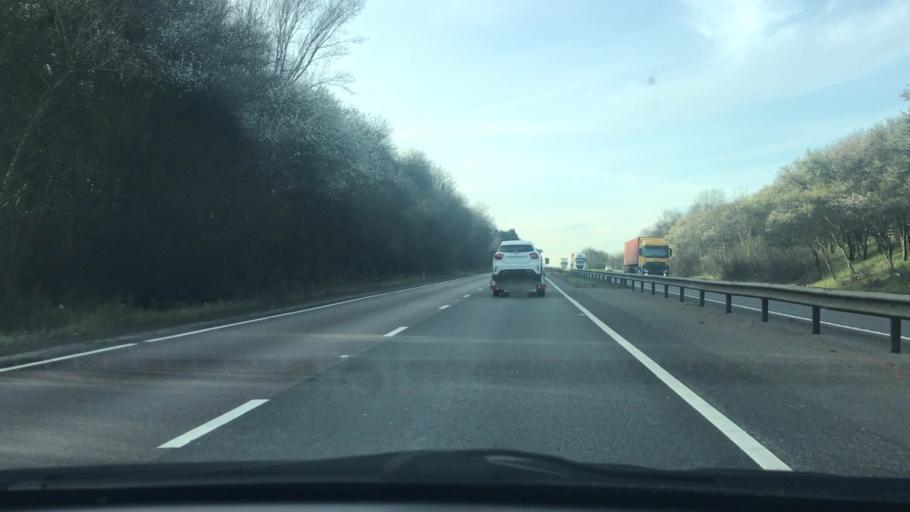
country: GB
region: England
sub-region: Nottinghamshire
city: Tuxford
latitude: 53.2278
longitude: -0.8920
